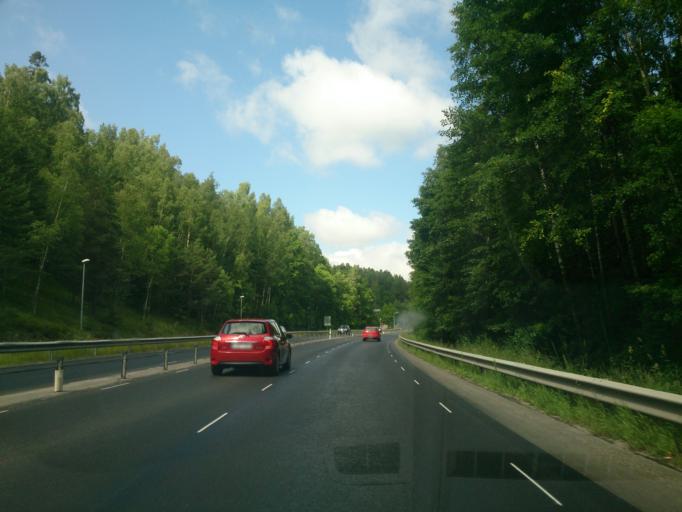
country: SE
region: OEstergoetland
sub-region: Norrkopings Kommun
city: Jursla
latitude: 58.6772
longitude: 16.1499
